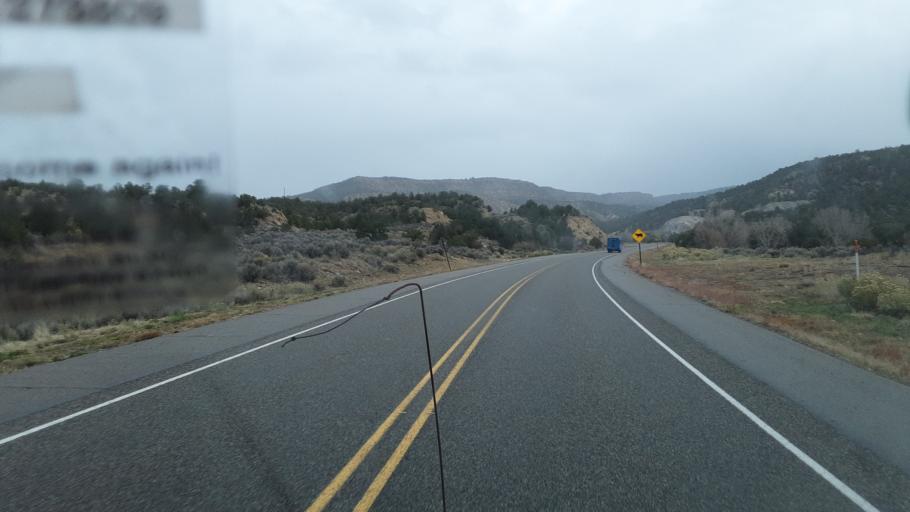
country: US
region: New Mexico
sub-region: Rio Arriba County
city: Santa Teresa
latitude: 36.3866
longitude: -106.4996
